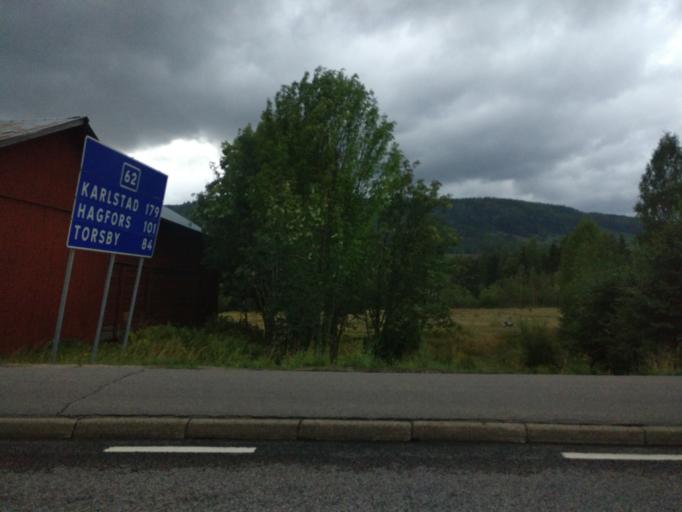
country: SE
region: Vaermland
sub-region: Torsby Kommun
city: Torsby
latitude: 60.7285
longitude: 12.8728
